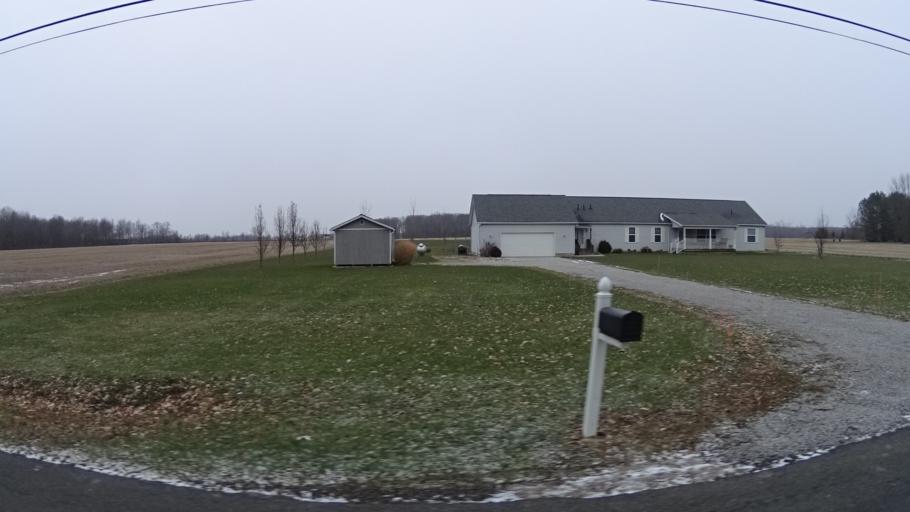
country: US
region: Ohio
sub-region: Lorain County
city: Lagrange
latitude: 41.2222
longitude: -82.1072
